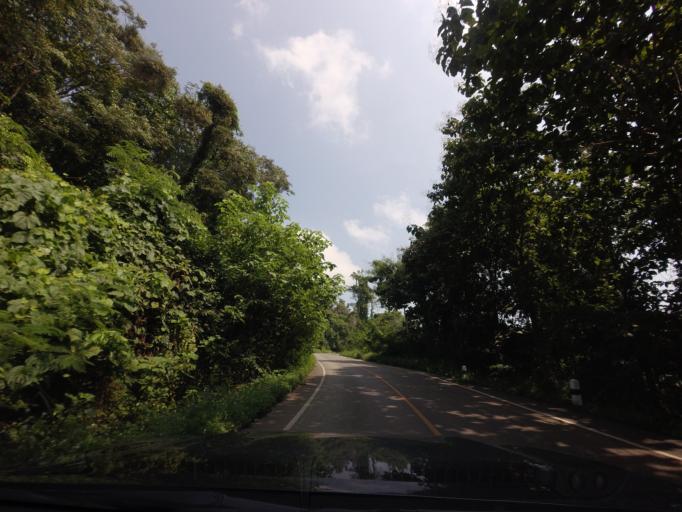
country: TH
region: Nan
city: Nan
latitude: 18.8478
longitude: 100.7788
